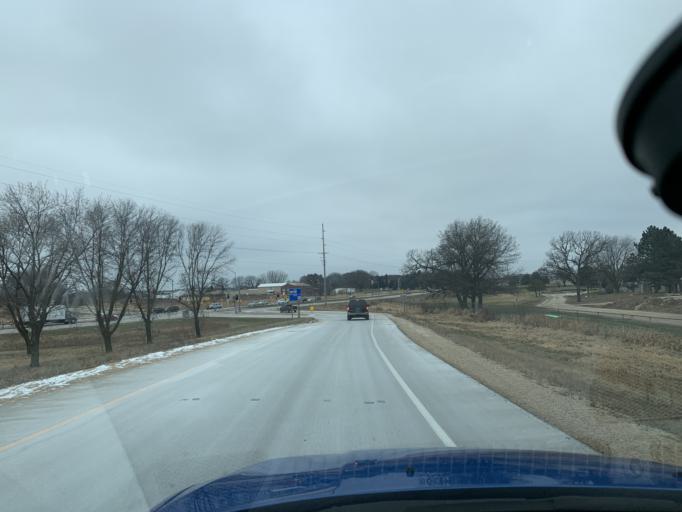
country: US
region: Wisconsin
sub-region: Dane County
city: Sun Prairie
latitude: 43.1769
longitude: -89.2493
